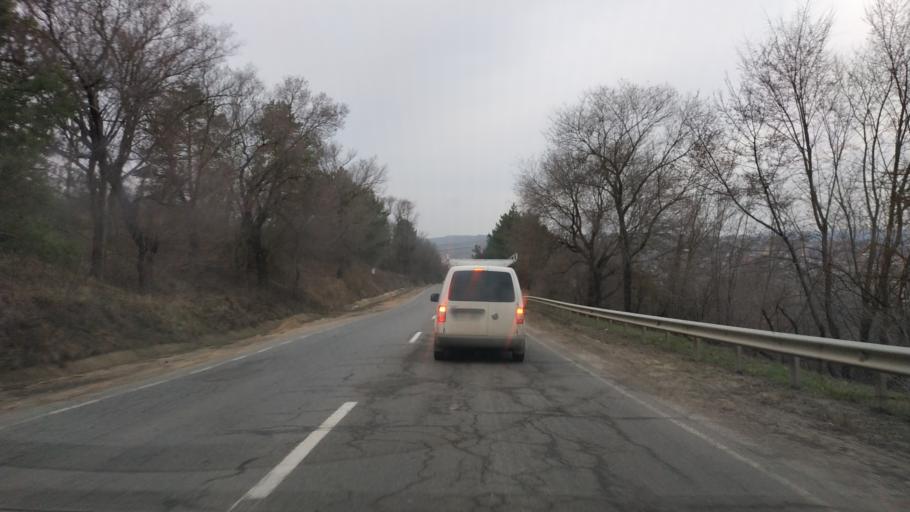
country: MD
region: Hincesti
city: Hincesti
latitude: 46.8288
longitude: 28.5741
